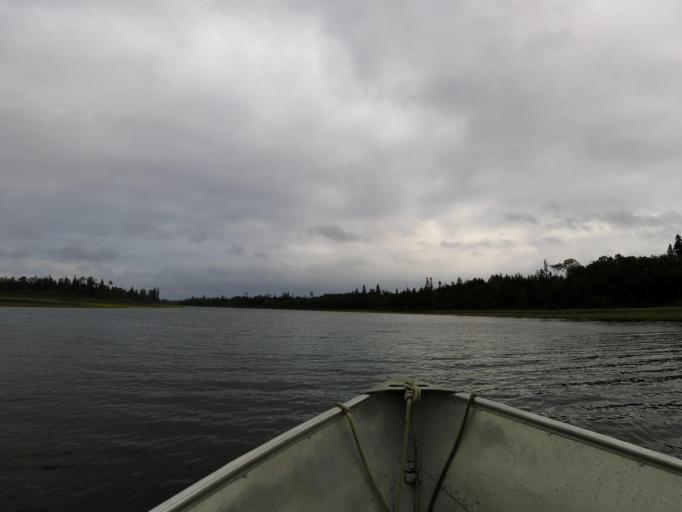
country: CA
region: Ontario
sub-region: Rainy River District
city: Atikokan
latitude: 49.5910
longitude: -91.3638
